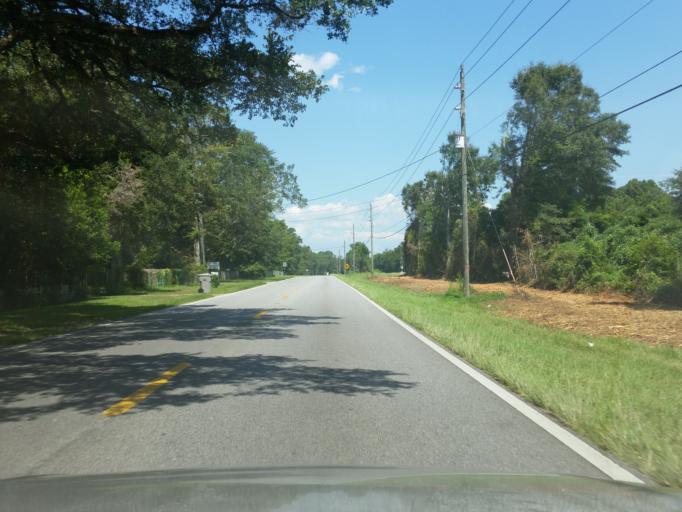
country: US
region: Florida
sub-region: Escambia County
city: Gonzalez
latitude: 30.5884
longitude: -87.3029
